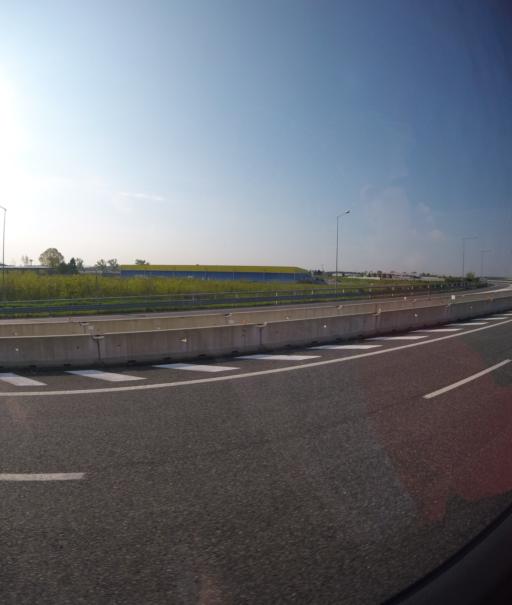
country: IT
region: Lombardy
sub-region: Provincia di Varese
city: Fagnano Olona-Bergoro
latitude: 45.6497
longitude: 8.8442
